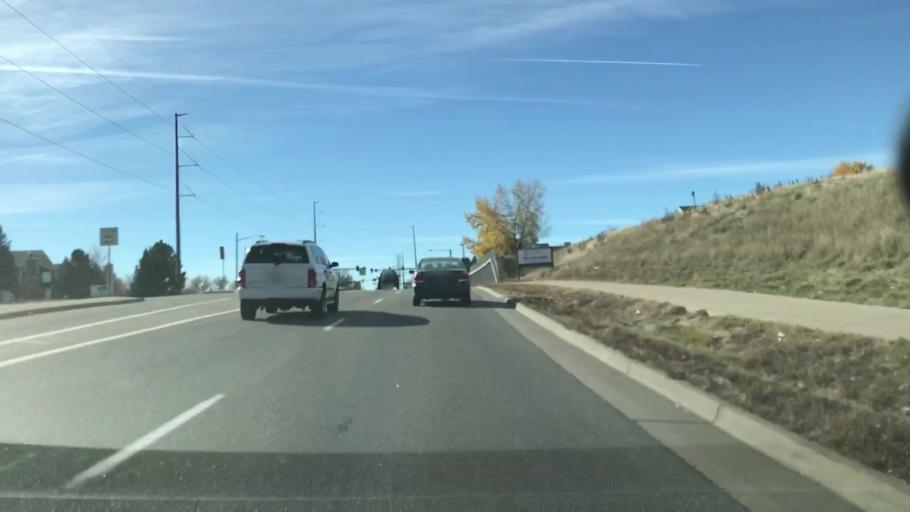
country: US
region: Colorado
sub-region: Arapahoe County
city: Glendale
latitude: 39.6798
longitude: -104.9036
